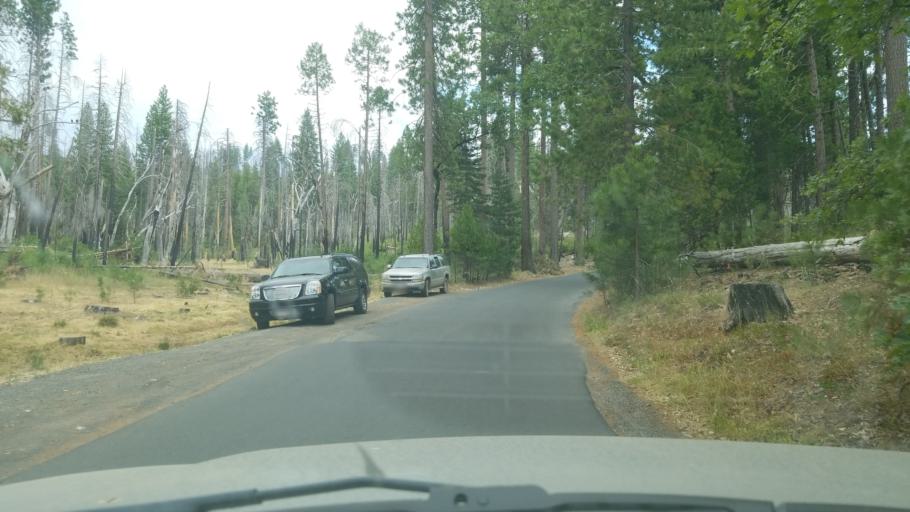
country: US
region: California
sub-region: Mariposa County
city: Yosemite Valley
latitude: 37.8752
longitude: -119.8578
